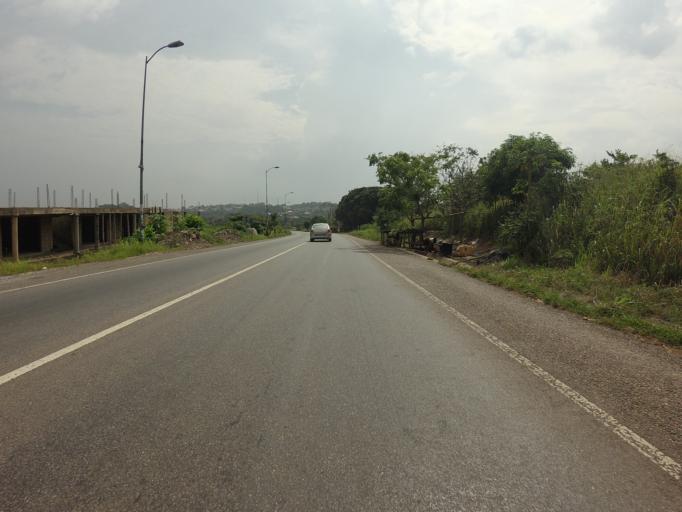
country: GH
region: Eastern
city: Aburi
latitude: 5.8257
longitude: -0.1857
